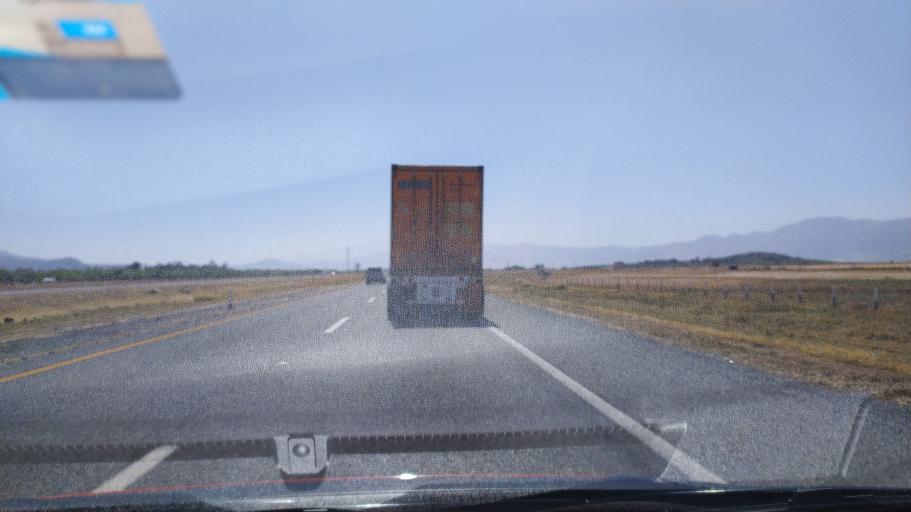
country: MX
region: Jalisco
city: Atoyac
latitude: 20.0267
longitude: -103.5301
